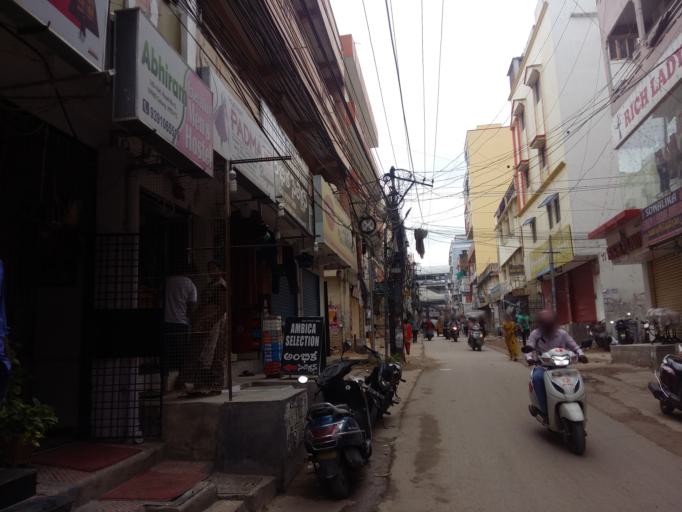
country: IN
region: Telangana
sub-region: Rangareddi
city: Kukatpalli
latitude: 17.4925
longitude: 78.4004
